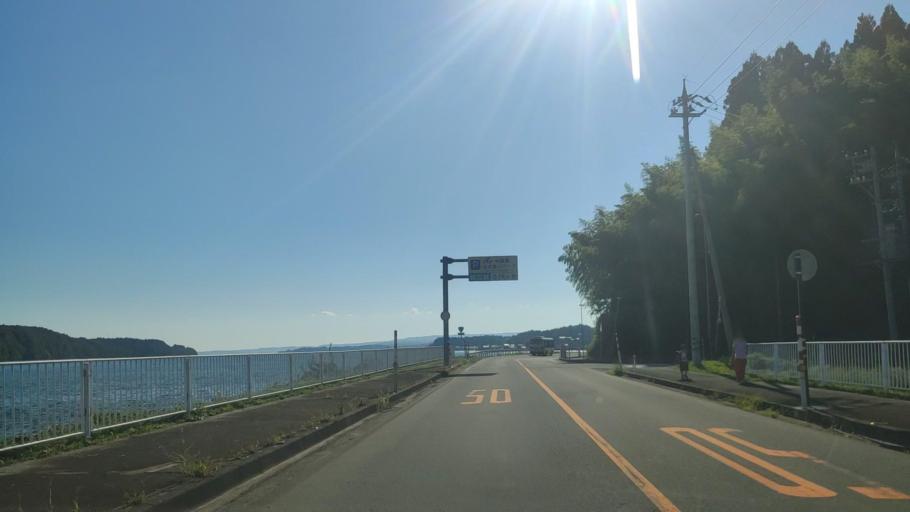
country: JP
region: Ishikawa
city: Nanao
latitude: 37.2357
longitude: 136.9585
